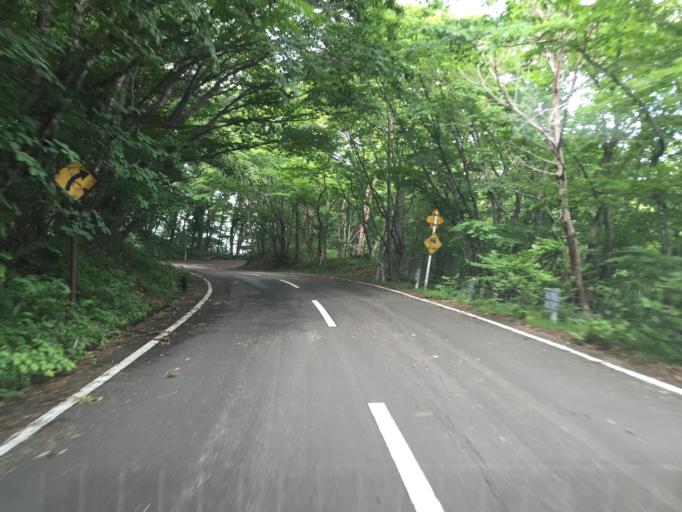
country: JP
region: Fukushima
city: Nihommatsu
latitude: 37.6631
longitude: 140.3239
